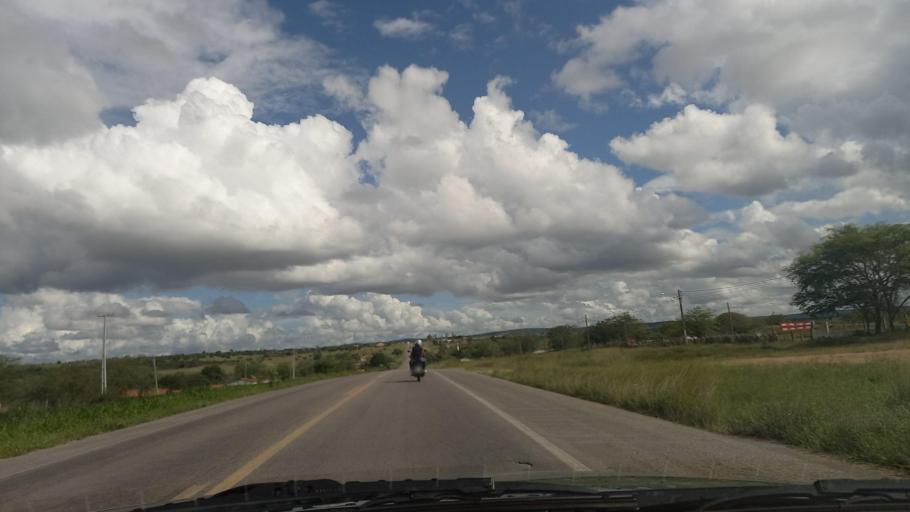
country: BR
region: Pernambuco
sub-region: Lajedo
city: Lajedo
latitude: -8.6185
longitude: -36.2997
